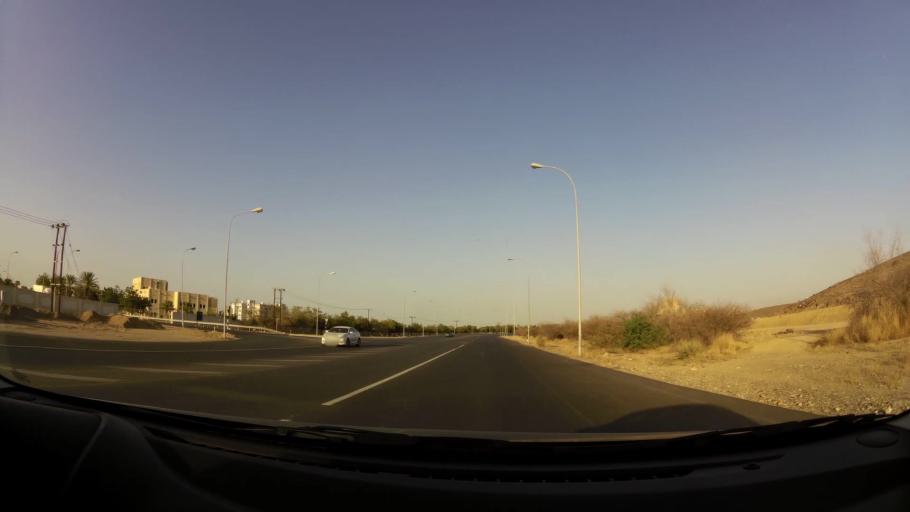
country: OM
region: Muhafazat Masqat
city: As Sib al Jadidah
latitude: 23.5818
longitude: 58.1701
